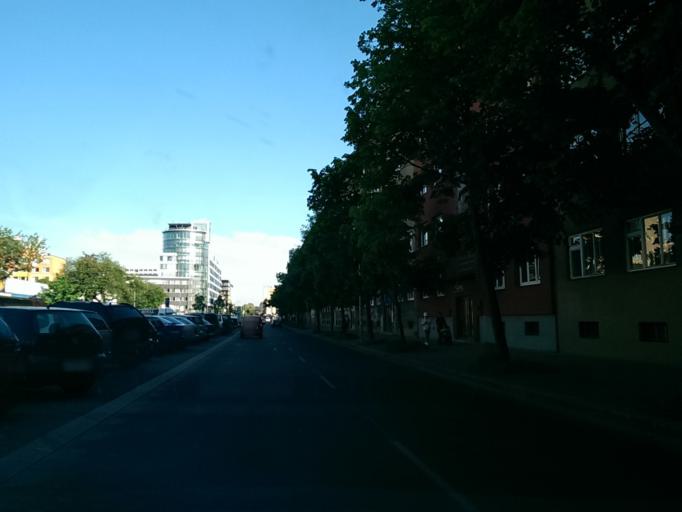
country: CZ
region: Praha
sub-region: Praha 2
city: Vysehrad
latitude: 50.0470
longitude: 14.4457
